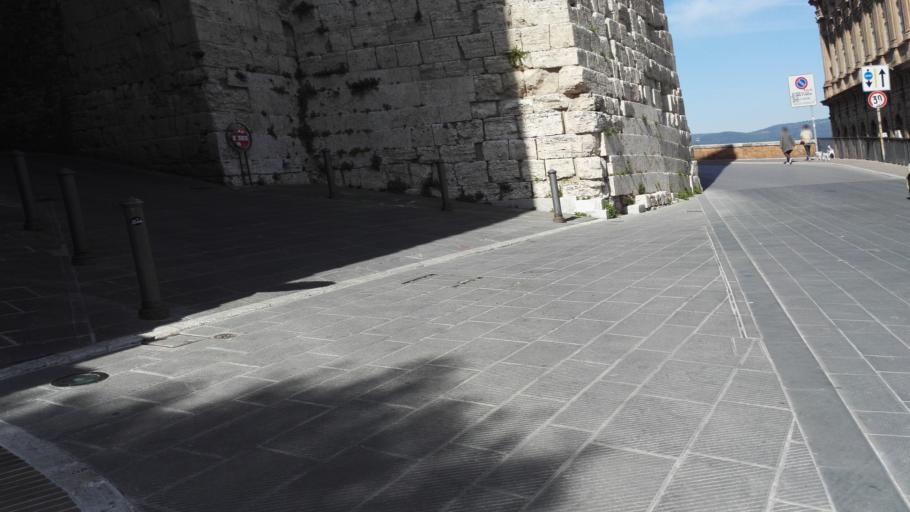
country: IT
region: Umbria
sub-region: Provincia di Perugia
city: Perugia
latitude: 43.1145
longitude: 12.3898
